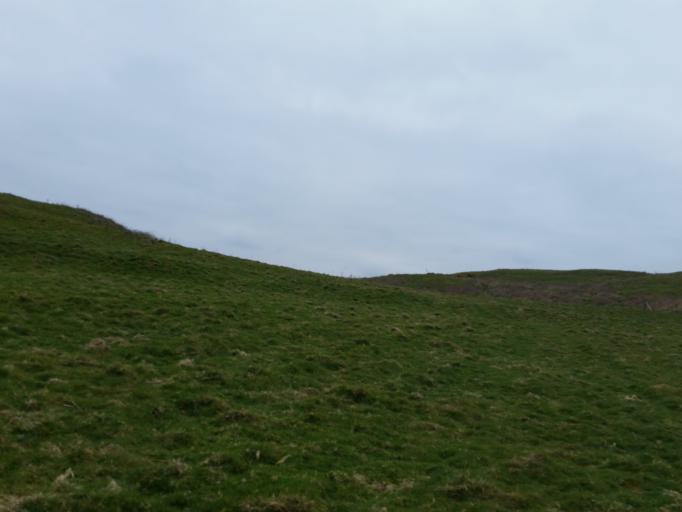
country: IE
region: Leinster
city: An Ros
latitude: 53.4896
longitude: -6.0127
